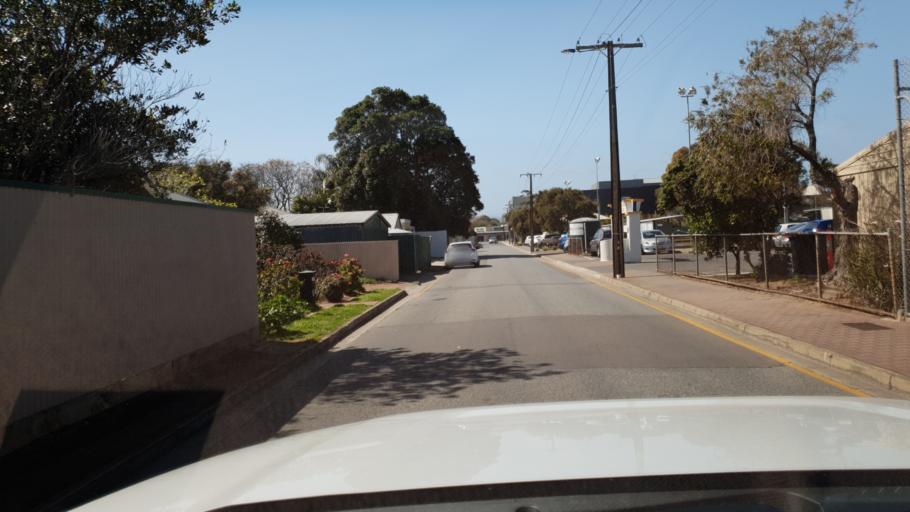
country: AU
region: South Australia
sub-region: Adelaide
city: Brighton
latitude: -35.0158
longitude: 138.5200
